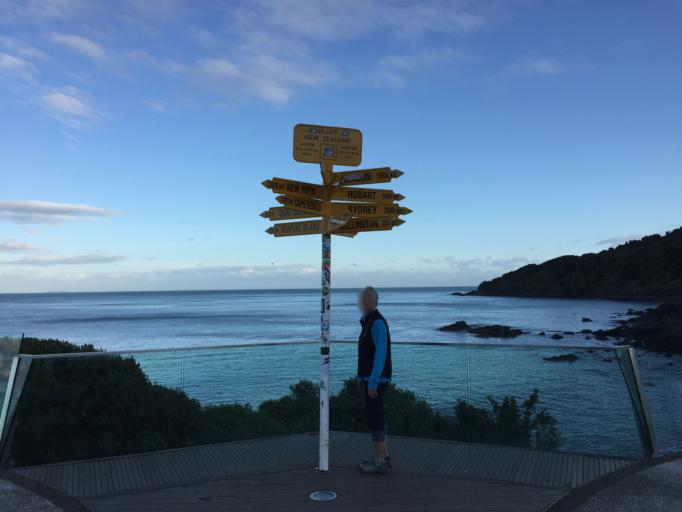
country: NZ
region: Southland
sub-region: Invercargill City
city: Bluff
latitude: -46.6134
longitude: 168.3572
